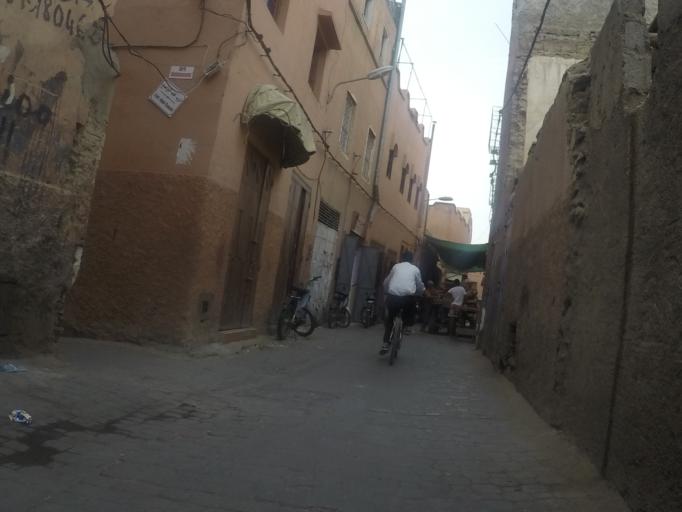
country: MA
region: Marrakech-Tensift-Al Haouz
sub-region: Marrakech
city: Marrakesh
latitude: 31.6287
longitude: -7.9811
